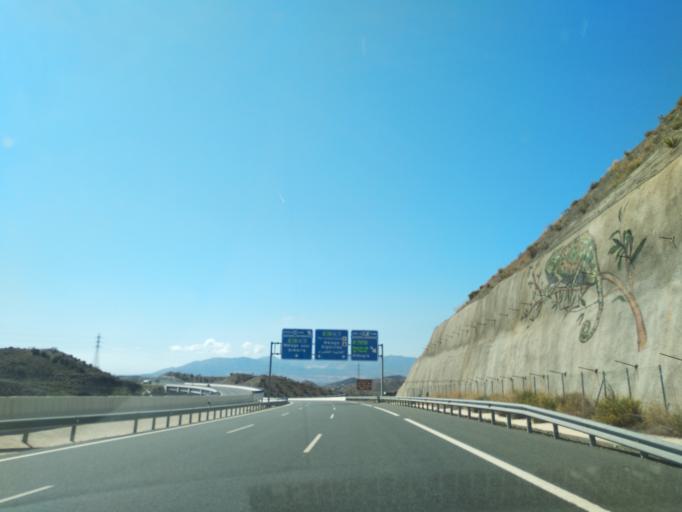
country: ES
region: Andalusia
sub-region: Provincia de Malaga
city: Almogia
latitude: 36.7666
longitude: -4.4867
